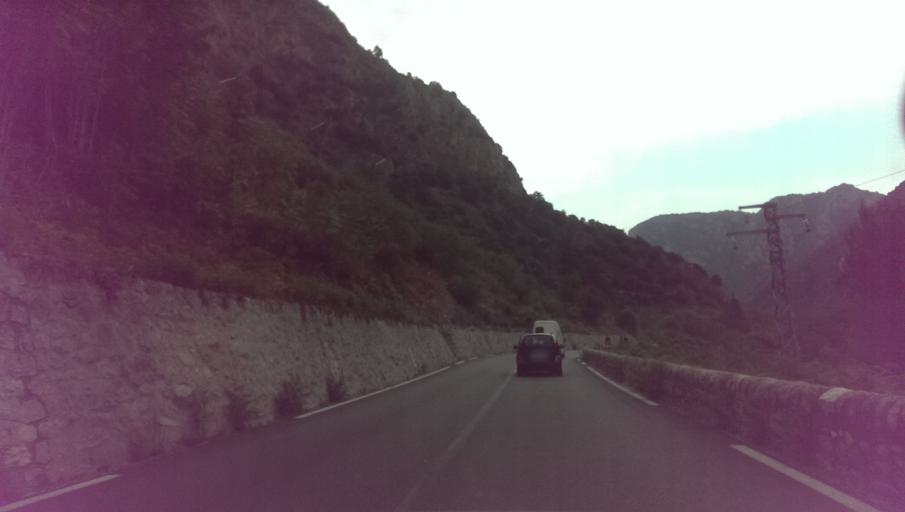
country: FR
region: Languedoc-Roussillon
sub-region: Departement des Pyrenees-Orientales
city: Vernet-les-Bains
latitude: 42.5836
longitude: 2.3551
